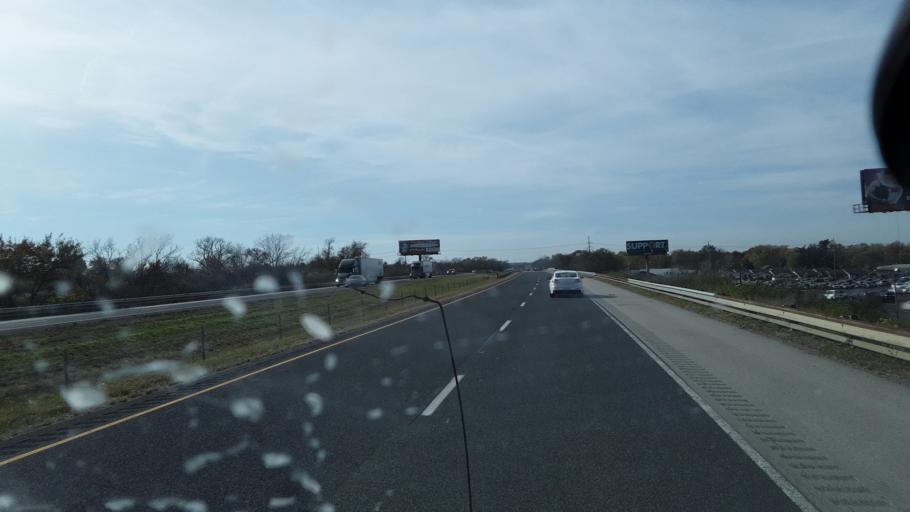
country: US
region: Indiana
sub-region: Vigo County
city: Terre Haute
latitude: 39.4319
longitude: -87.3910
